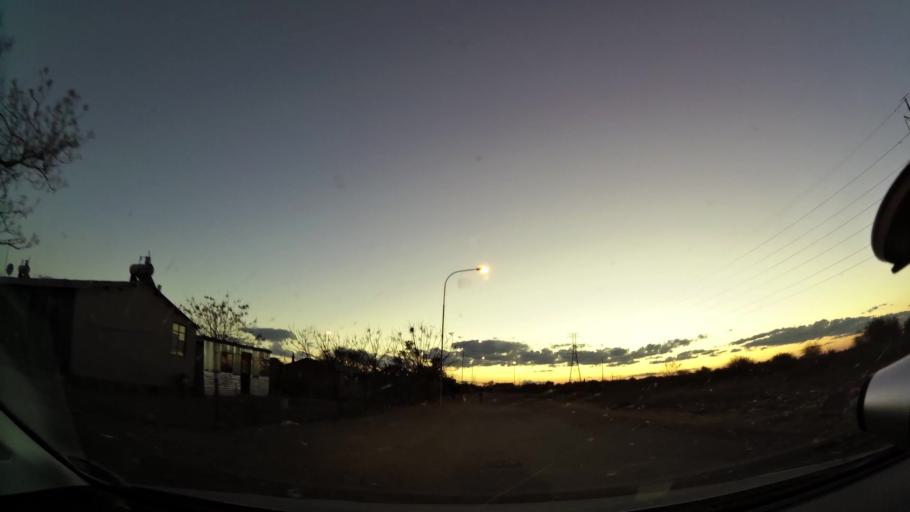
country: ZA
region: Northern Cape
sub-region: Frances Baard District Municipality
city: Kimberley
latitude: -28.7127
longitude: 24.7623
